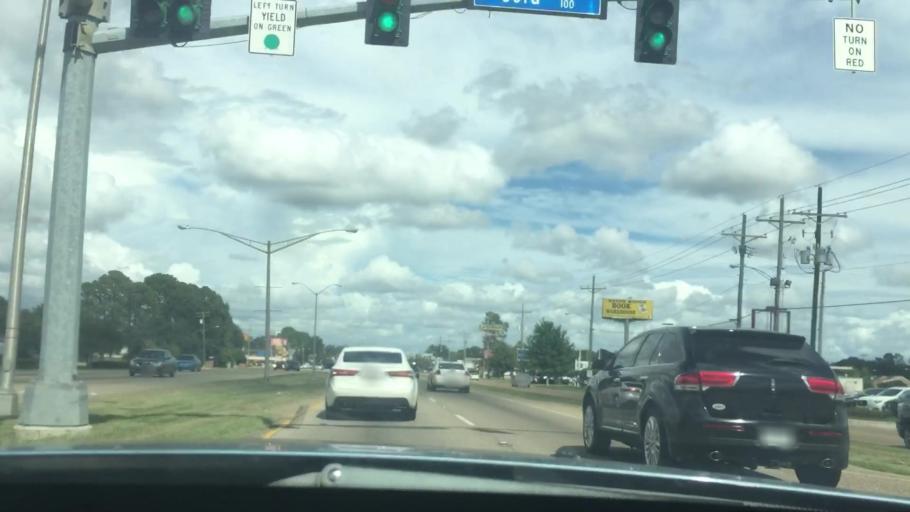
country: US
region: Louisiana
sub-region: East Baton Rouge Parish
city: Westminster
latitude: 30.4542
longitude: -91.0878
